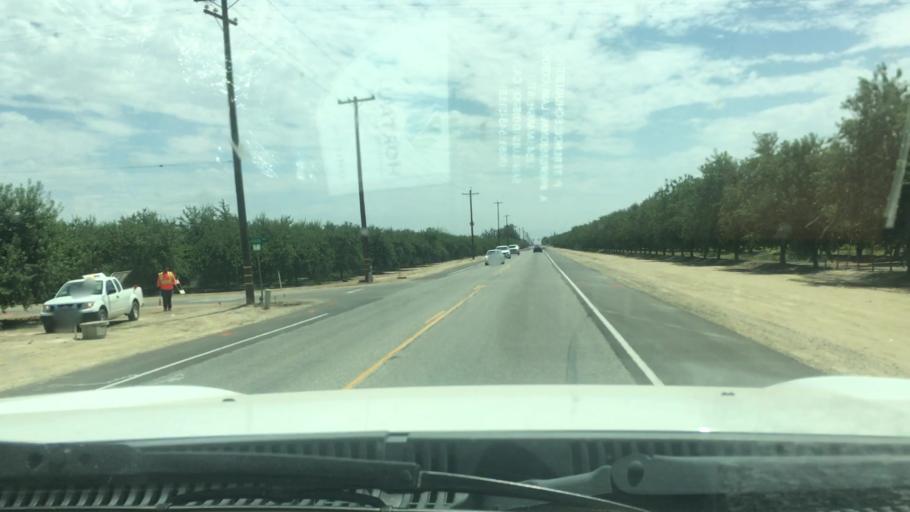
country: US
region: California
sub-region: Kern County
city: Wasco
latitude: 35.5580
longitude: -119.3411
